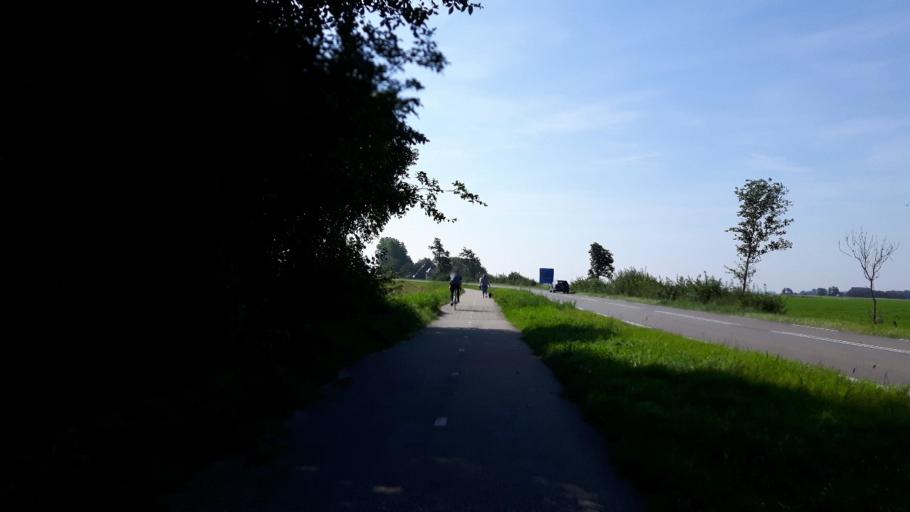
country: NL
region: Friesland
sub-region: Gemeente Dongeradeel
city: Holwerd
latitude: 53.3709
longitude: 5.8950
